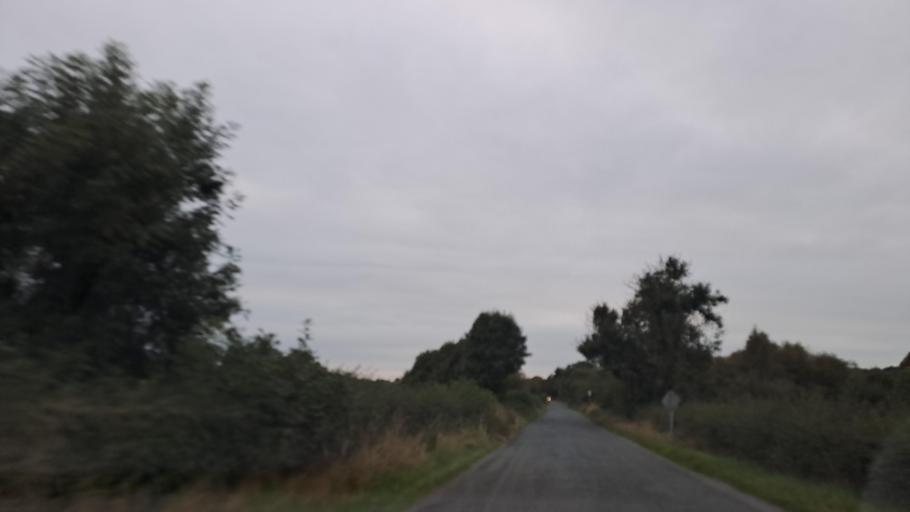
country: IE
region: Ulster
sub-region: County Monaghan
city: Carrickmacross
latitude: 54.0232
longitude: -6.7852
